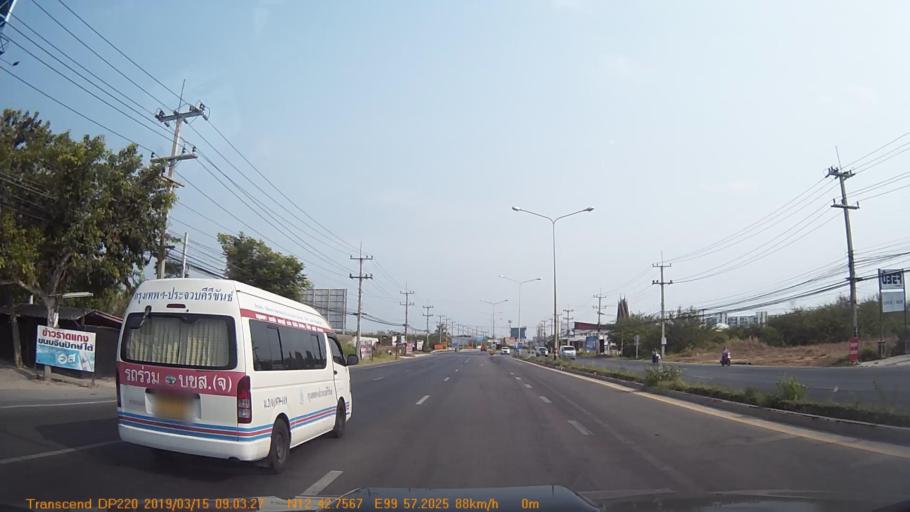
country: TH
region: Phetchaburi
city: Cha-am
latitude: 12.7133
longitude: 99.9531
